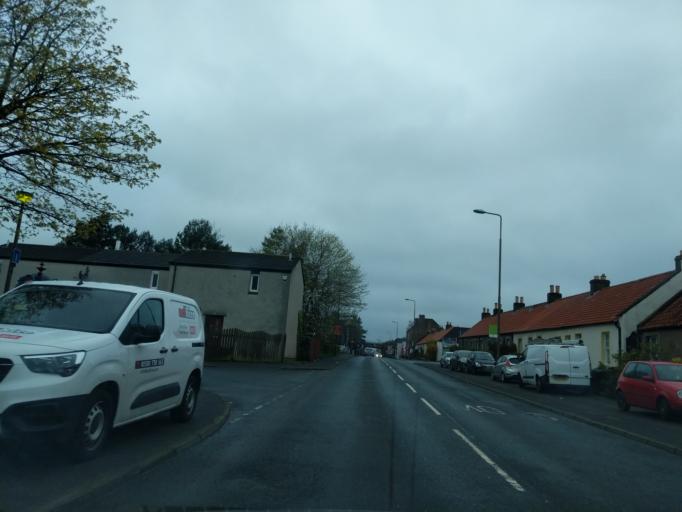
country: GB
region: Scotland
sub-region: East Lothian
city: Musselburgh
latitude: 55.9353
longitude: -3.0891
